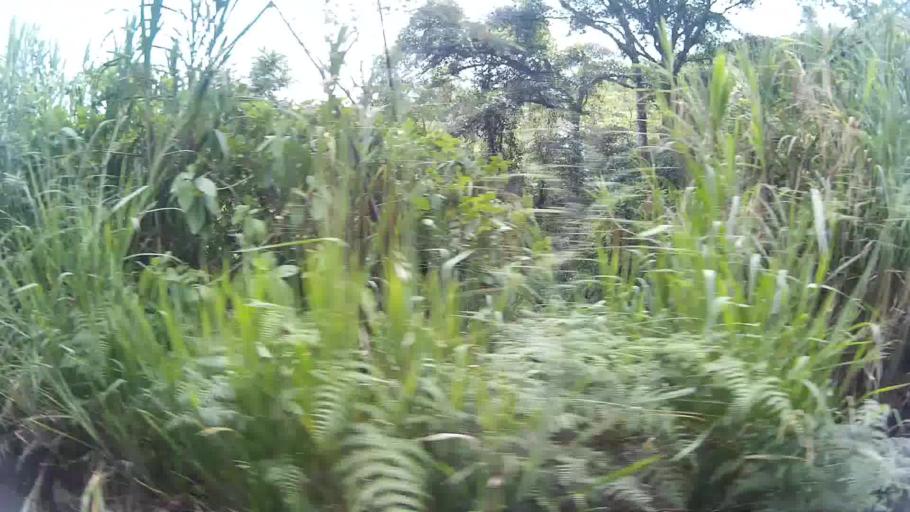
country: CO
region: Caldas
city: Belalcazar
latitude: 4.9448
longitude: -75.8389
